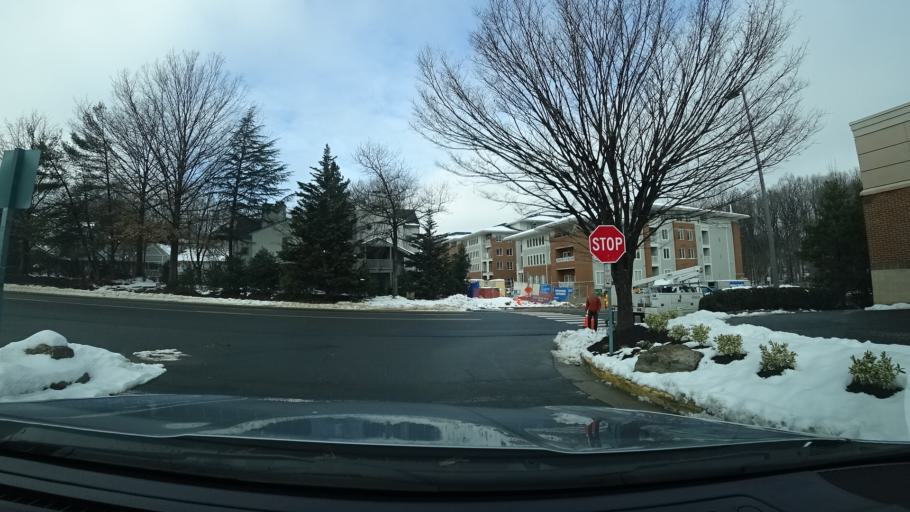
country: US
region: Virginia
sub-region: Fairfax County
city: Reston
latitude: 38.9378
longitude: -77.3623
